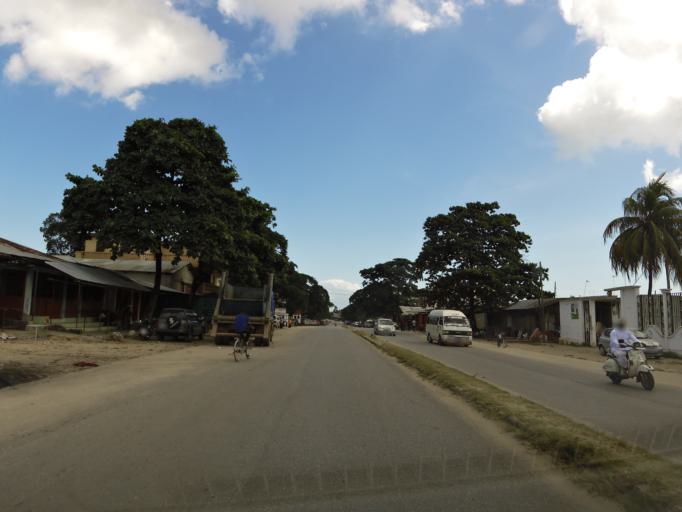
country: TZ
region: Zanzibar Urban/West
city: Zanzibar
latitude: -6.1640
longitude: 39.2206
